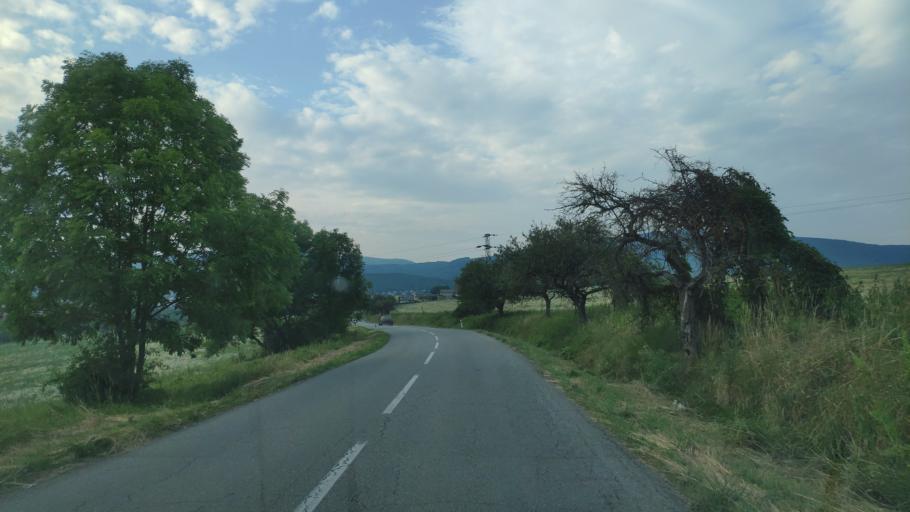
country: SK
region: Kosicky
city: Medzev
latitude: 48.6991
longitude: 20.9740
